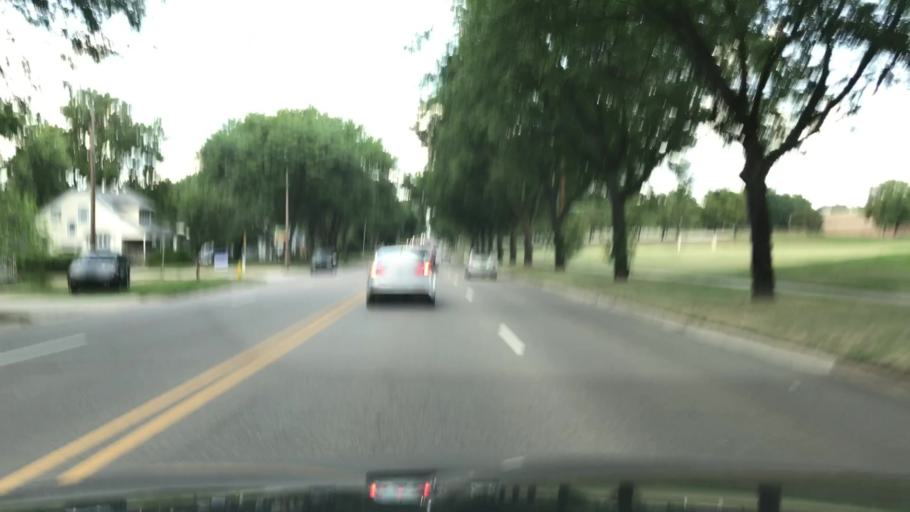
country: US
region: Michigan
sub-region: Kent County
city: Grand Rapids
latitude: 42.9876
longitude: -85.6398
